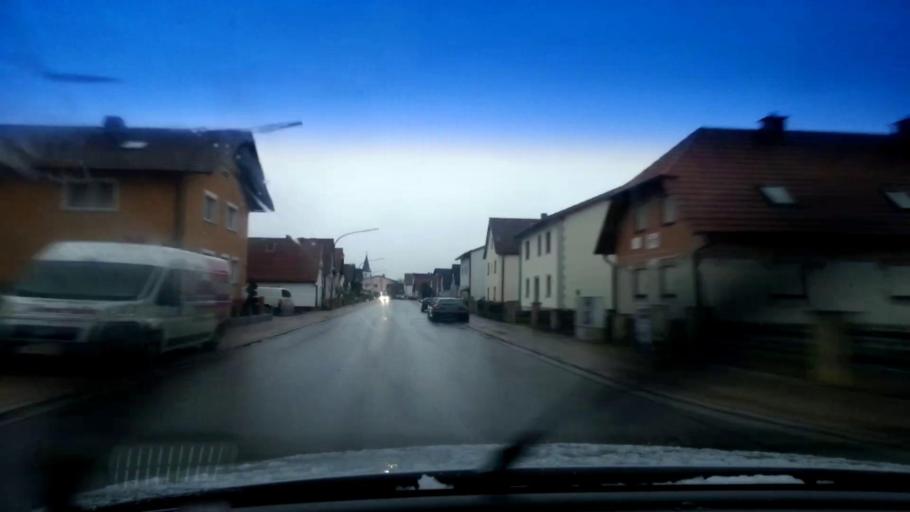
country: DE
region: Bavaria
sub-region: Upper Franconia
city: Oberhaid
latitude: 49.9325
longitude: 10.8094
